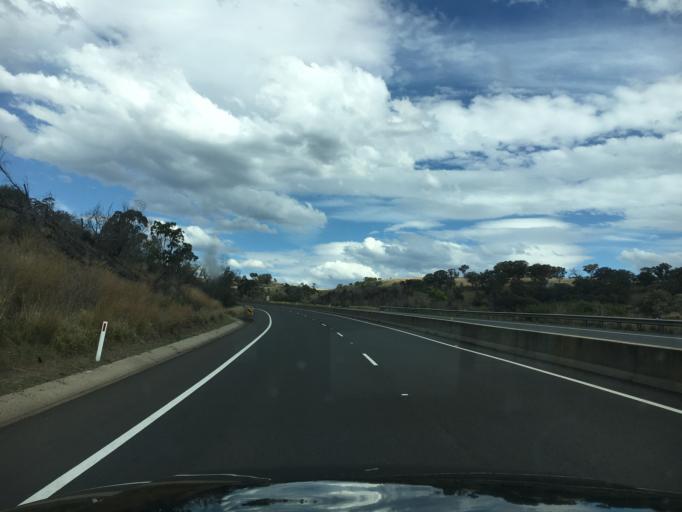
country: AU
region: New South Wales
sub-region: Liverpool Plains
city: Quirindi
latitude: -31.7346
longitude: 150.7855
